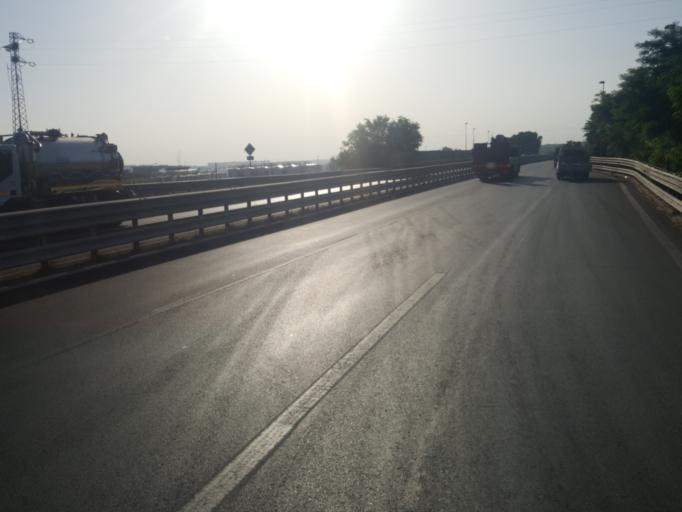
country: IT
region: Apulia
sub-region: Provincia di Foggia
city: Cerignola
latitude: 41.2809
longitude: 15.8942
